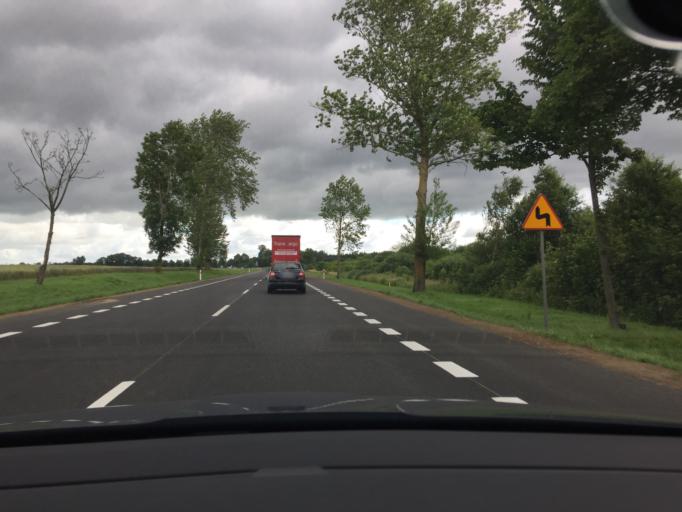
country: PL
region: West Pomeranian Voivodeship
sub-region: Powiat bialogardzki
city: Bialogard
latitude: 54.0686
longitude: 15.9473
